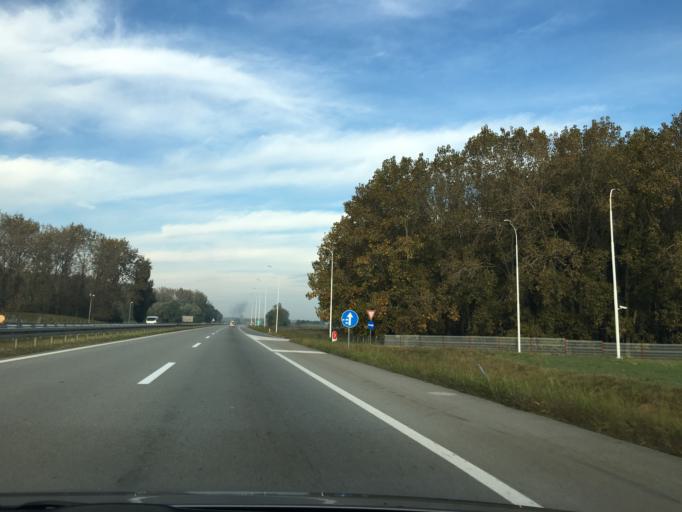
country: RS
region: Autonomna Pokrajina Vojvodina
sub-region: Juznobacki Okrug
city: Petrovaradin
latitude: 45.2763
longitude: 19.9217
